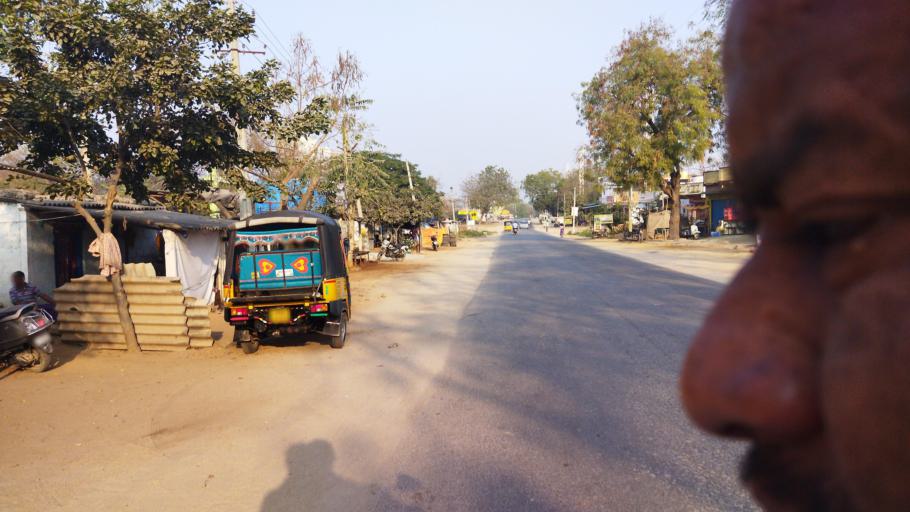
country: IN
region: Telangana
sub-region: Nalgonda
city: Nalgonda
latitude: 17.2348
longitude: 79.1232
